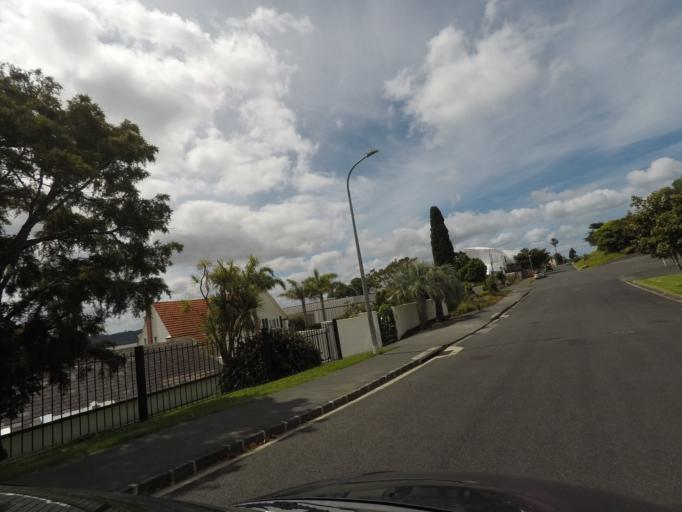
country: NZ
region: Auckland
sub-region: Auckland
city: Auckland
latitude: -36.8462
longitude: 174.7251
